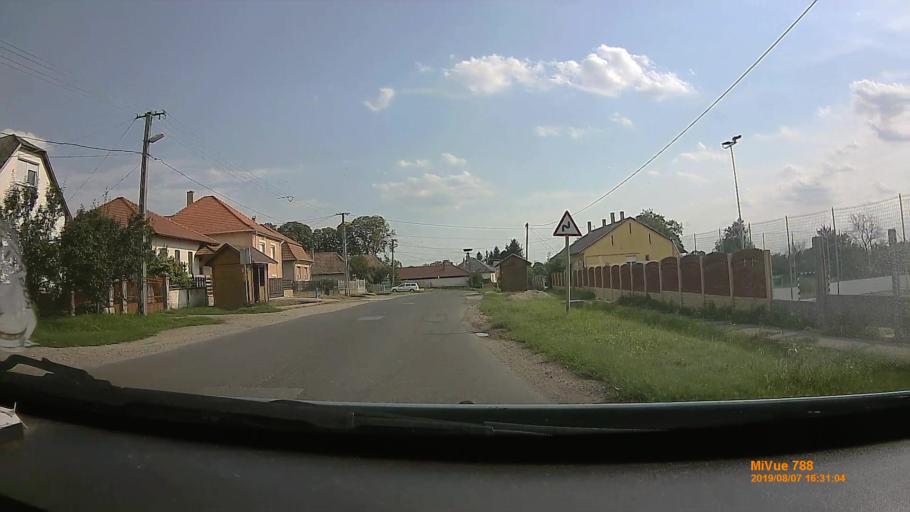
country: HU
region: Borsod-Abauj-Zemplen
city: Gonc
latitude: 48.4518
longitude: 21.2421
